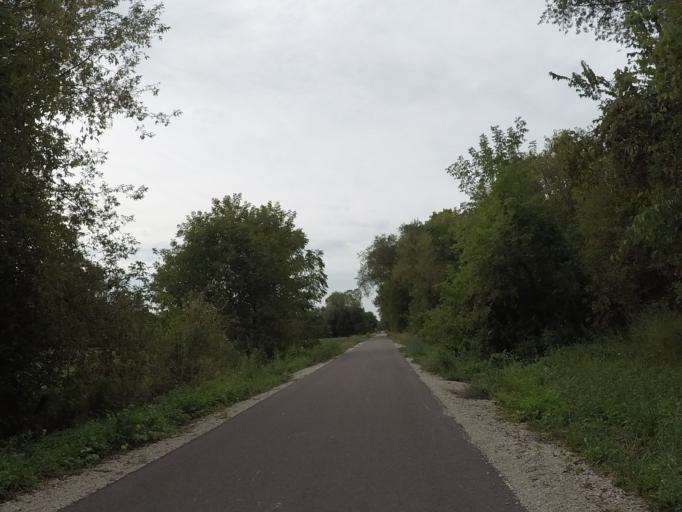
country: US
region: Wisconsin
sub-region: Sauk County
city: Prairie du Sac
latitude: 43.3557
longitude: -89.7406
